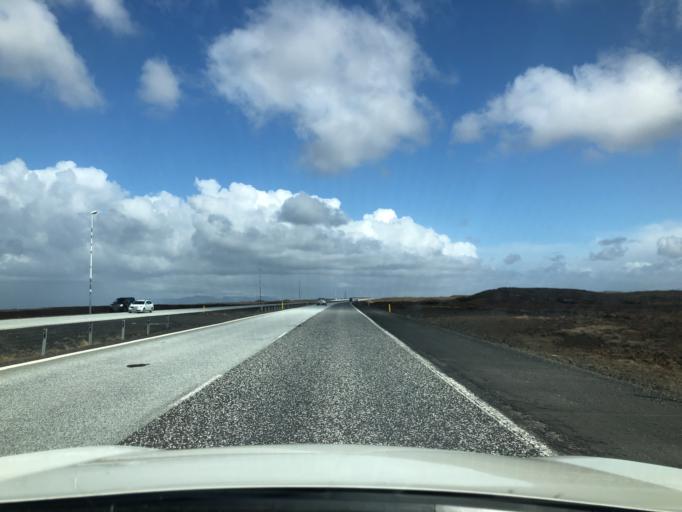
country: IS
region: Southern Peninsula
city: Vogar
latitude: 63.9929
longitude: -22.2825
